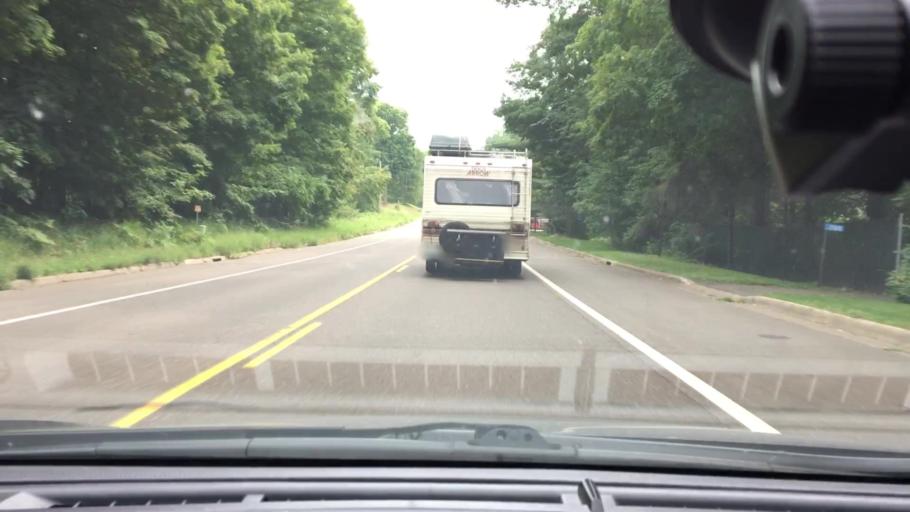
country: US
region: Minnesota
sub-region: Crow Wing County
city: Crosby
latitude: 46.4104
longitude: -93.8600
